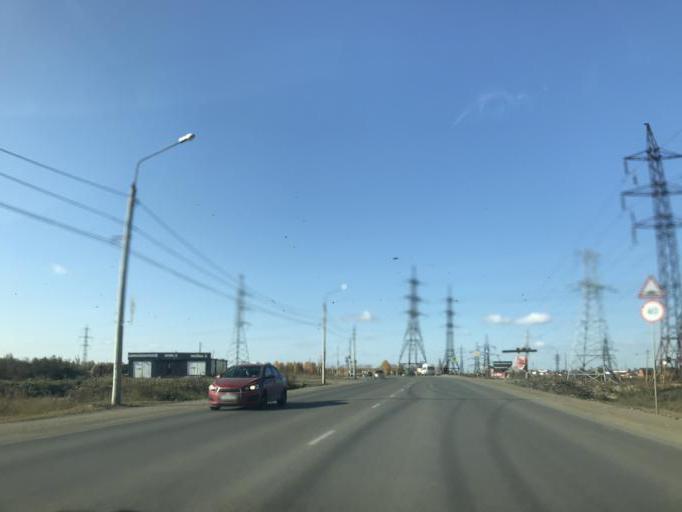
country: RU
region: Chelyabinsk
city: Roshchino
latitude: 55.2240
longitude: 61.2922
